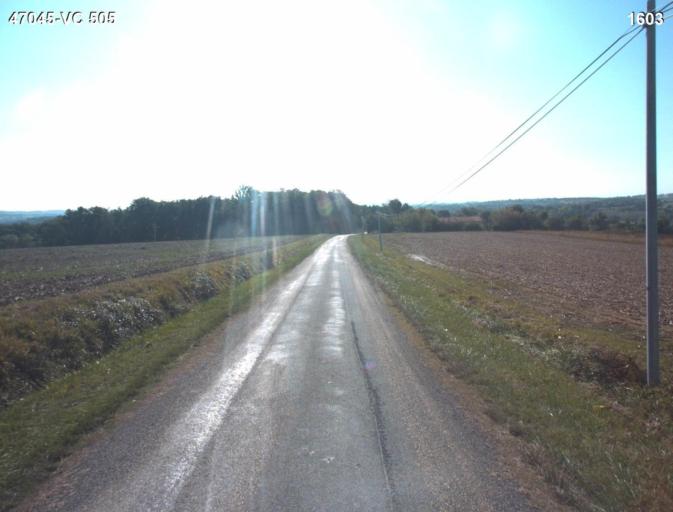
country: FR
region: Aquitaine
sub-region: Departement du Lot-et-Garonne
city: Nerac
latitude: 44.1500
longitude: 0.4149
